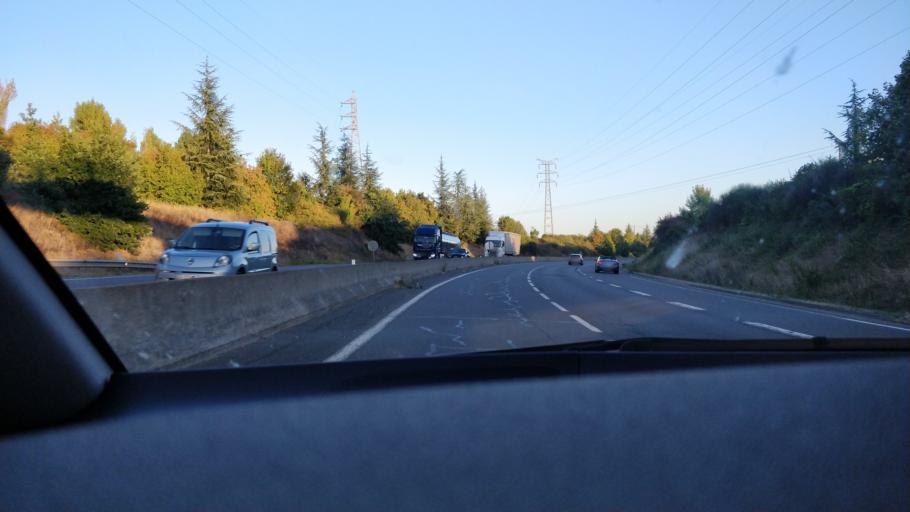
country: FR
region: Poitou-Charentes
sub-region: Departement de la Charente
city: Gond-Pontouvre
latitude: 45.6957
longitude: 0.1874
